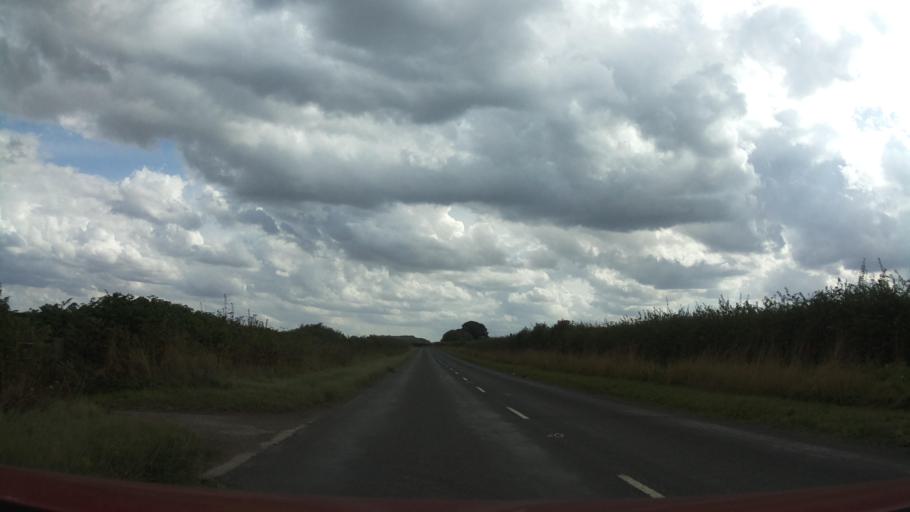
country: GB
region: England
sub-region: North Yorkshire
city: Ripon
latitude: 54.1690
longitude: -1.5509
